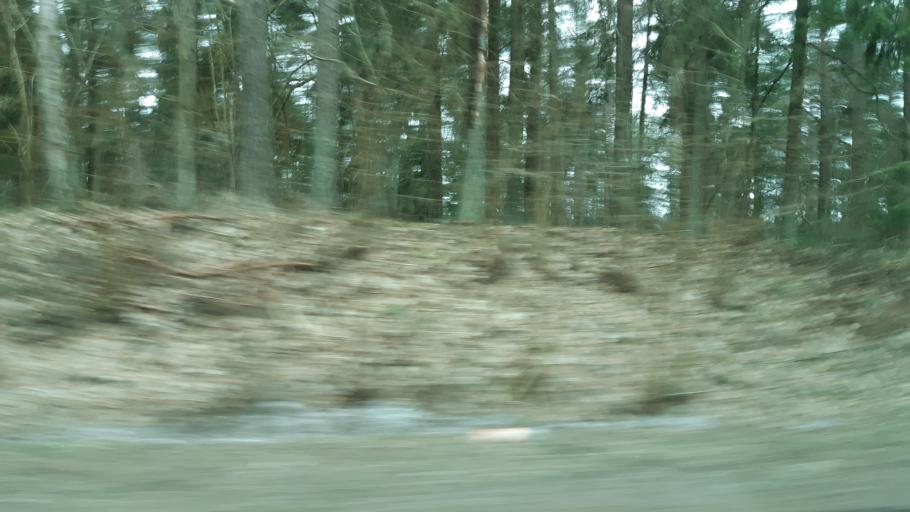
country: PL
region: Podlasie
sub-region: Suwalki
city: Suwalki
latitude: 54.3068
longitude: 22.9585
